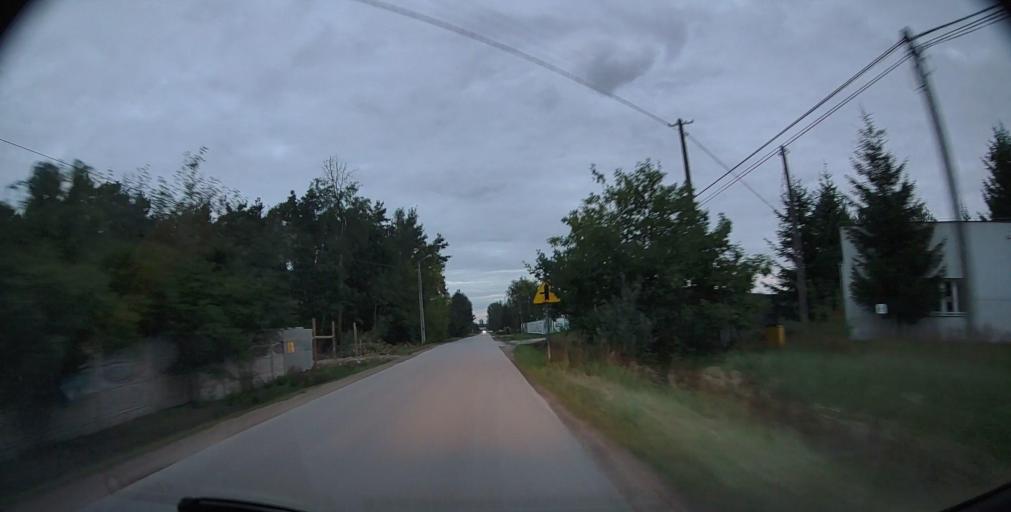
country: PL
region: Masovian Voivodeship
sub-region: Powiat radomski
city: Jedlinsk
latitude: 51.4647
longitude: 21.1277
